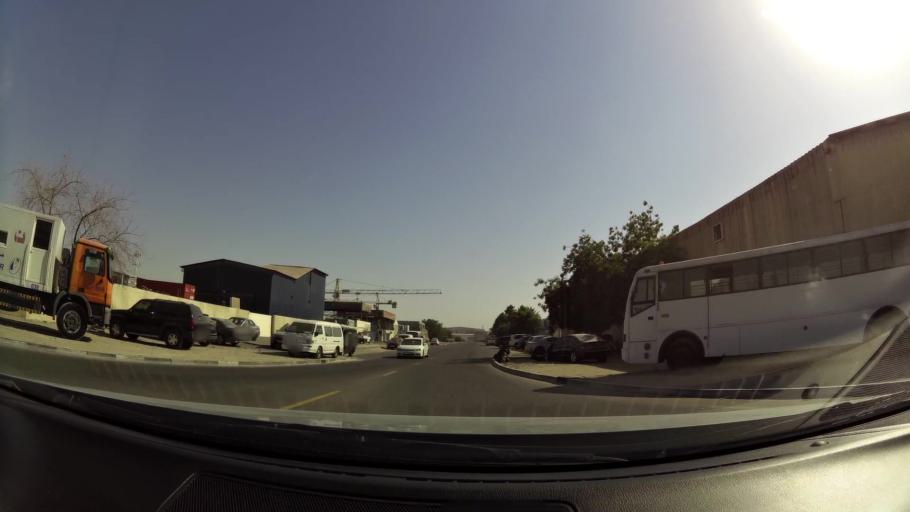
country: AE
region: Dubai
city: Dubai
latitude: 25.1323
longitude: 55.2228
